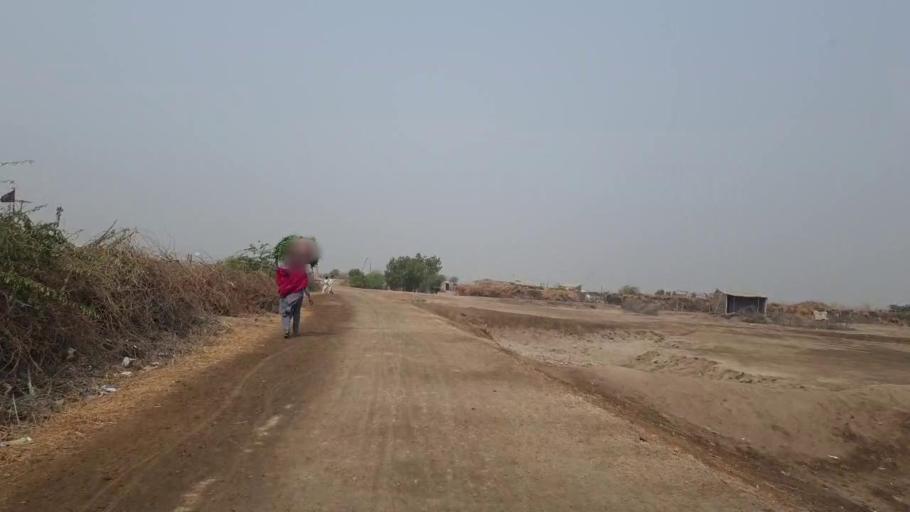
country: PK
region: Sindh
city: Kario
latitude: 24.6609
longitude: 68.6395
